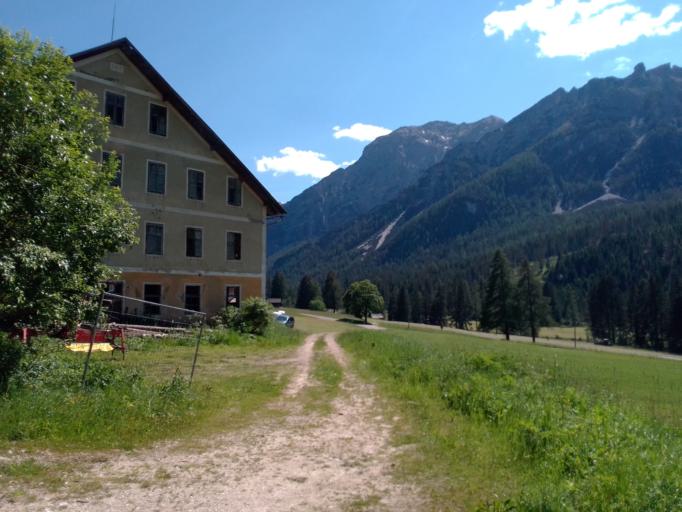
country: IT
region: Trentino-Alto Adige
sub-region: Bolzano
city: Braies
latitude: 46.7061
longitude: 12.1559
